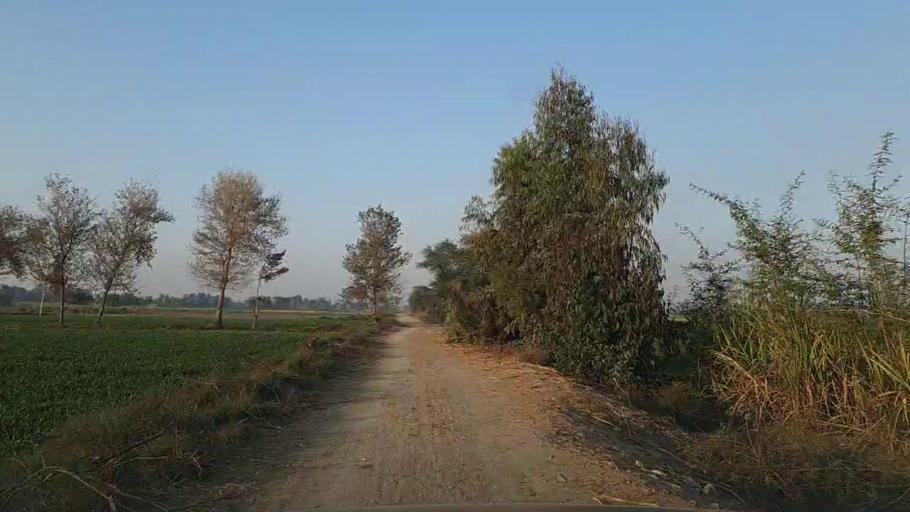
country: PK
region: Sindh
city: Daur
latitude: 26.4847
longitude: 68.4180
